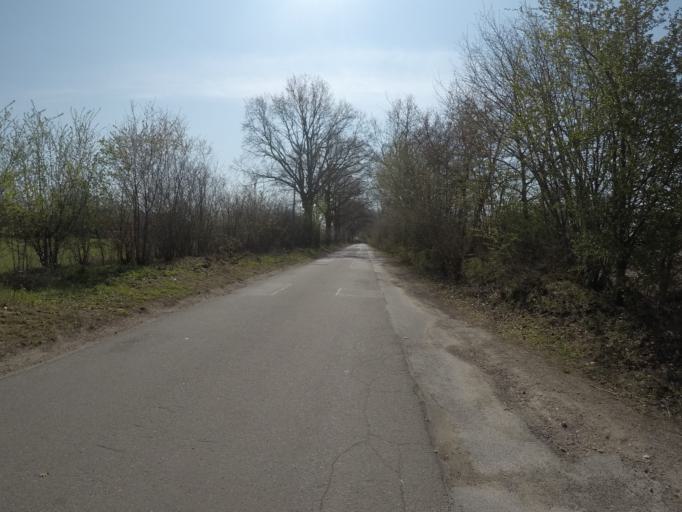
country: DE
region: Schleswig-Holstein
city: Halstenbek
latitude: 53.5935
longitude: 9.8164
